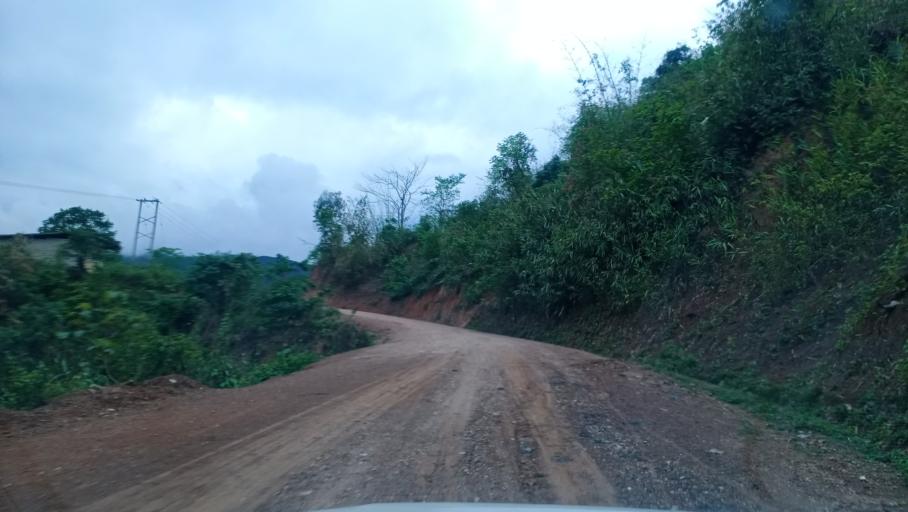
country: LA
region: Phongsali
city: Khoa
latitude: 21.2013
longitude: 102.6881
